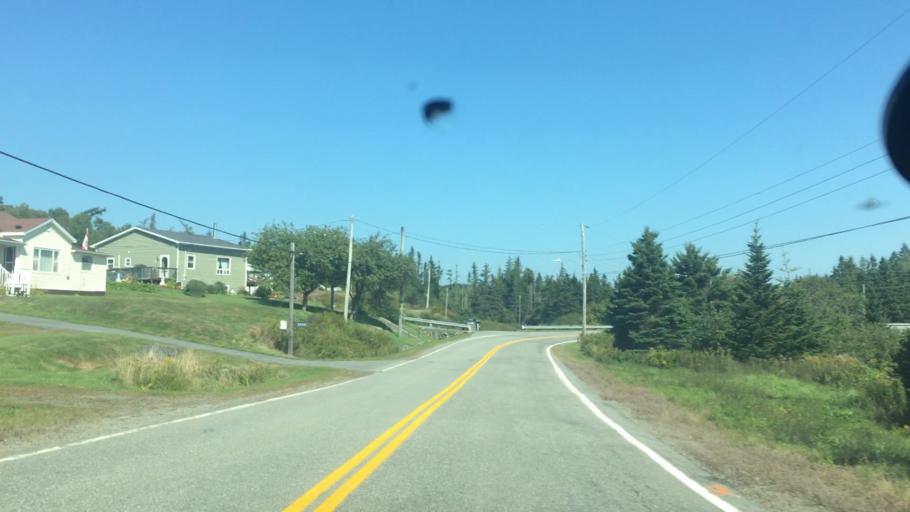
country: CA
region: Nova Scotia
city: New Glasgow
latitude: 44.9153
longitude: -62.3846
